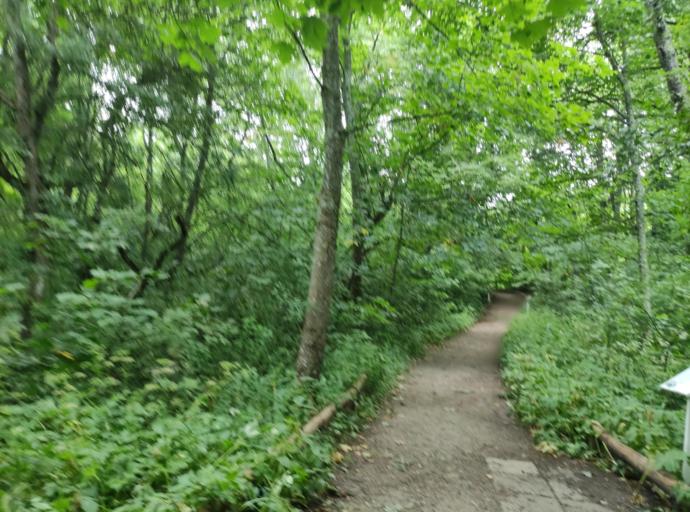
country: BG
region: Sofia-Capital
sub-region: Stolichna Obshtina
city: Sofia
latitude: 42.6275
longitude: 23.2277
